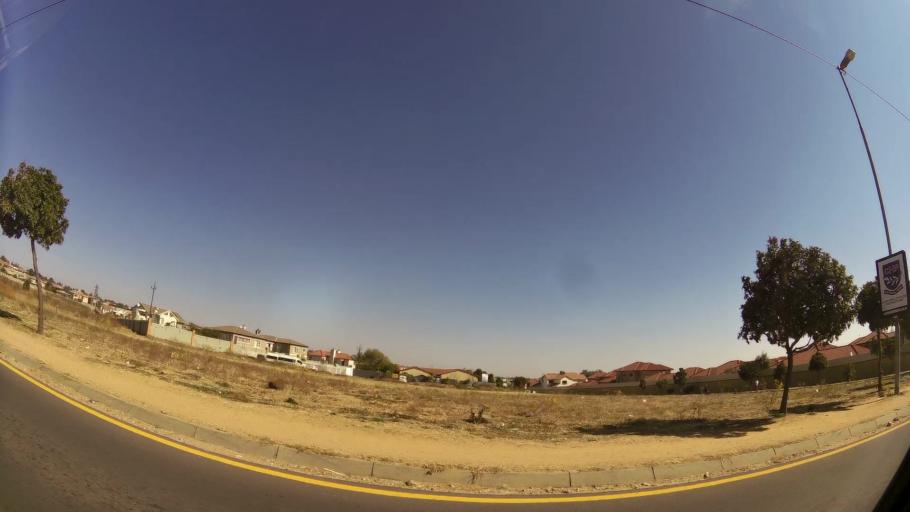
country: ZA
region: Gauteng
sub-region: City of Johannesburg Metropolitan Municipality
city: Midrand
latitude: -25.9657
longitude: 28.1018
